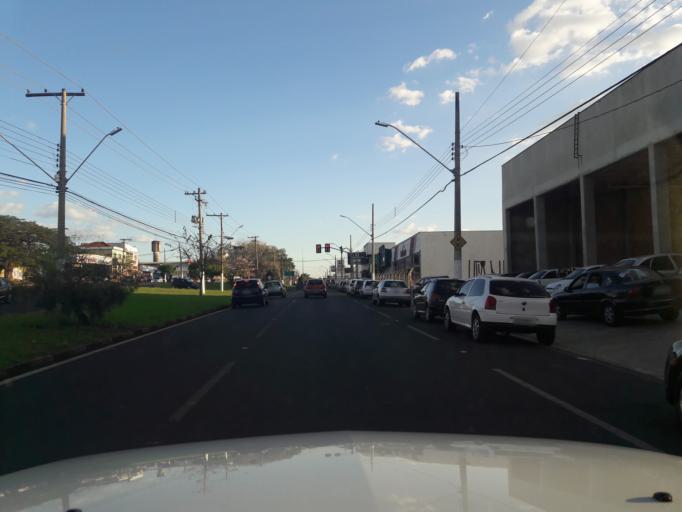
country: BR
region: Sao Paulo
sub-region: Moji-Guacu
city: Mogi-Gaucu
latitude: -22.3895
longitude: -46.9448
